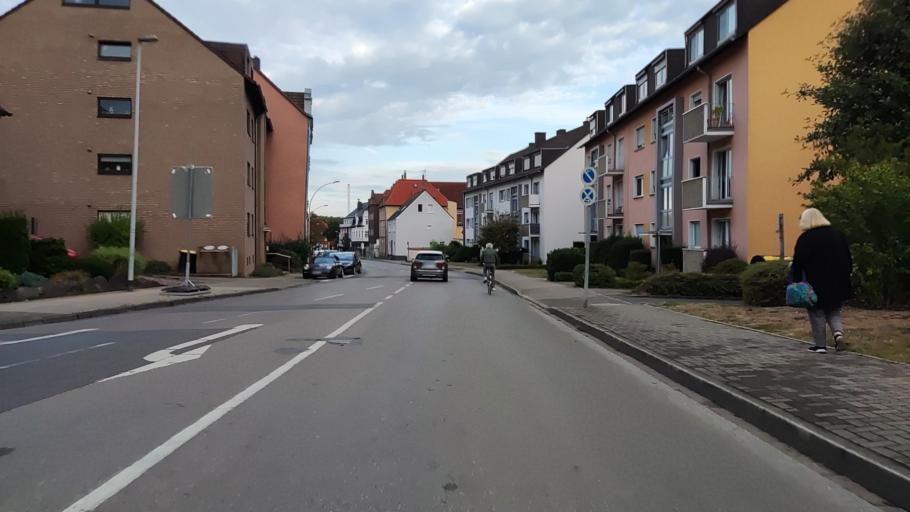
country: DE
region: North Rhine-Westphalia
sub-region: Regierungsbezirk Arnsberg
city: Herne
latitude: 51.5407
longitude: 7.2392
